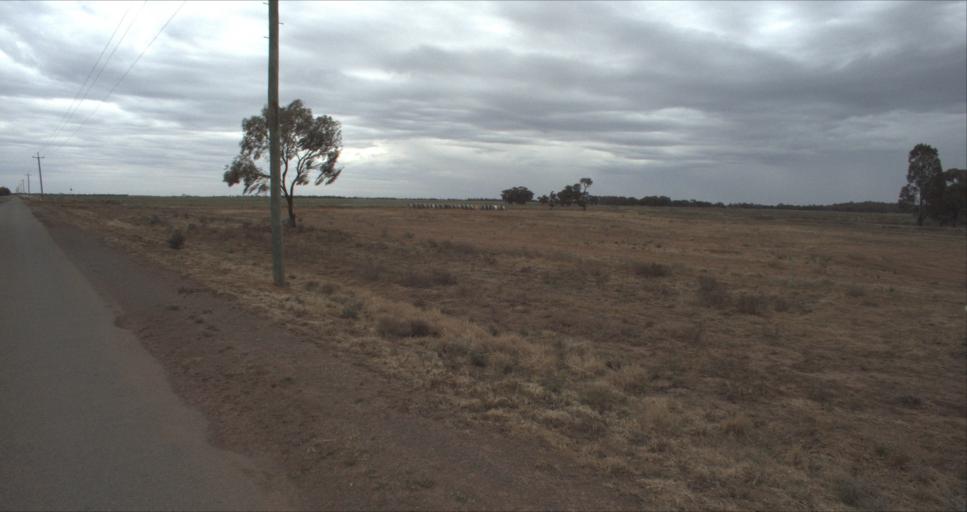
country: AU
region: New South Wales
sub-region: Leeton
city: Leeton
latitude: -34.4219
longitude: 146.3383
